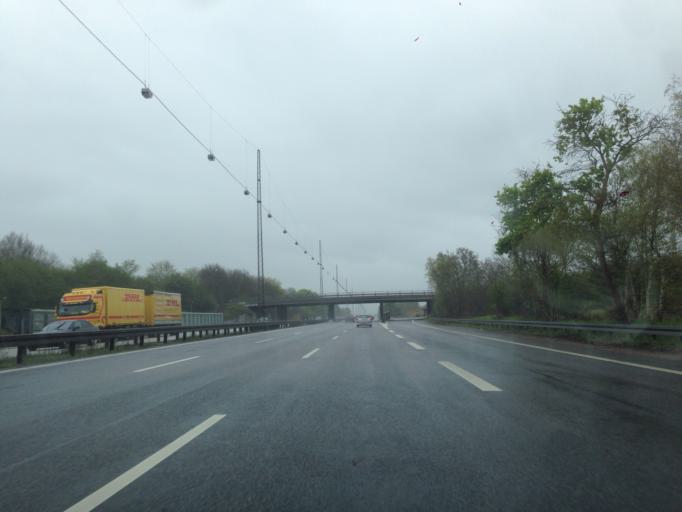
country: DK
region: Capital Region
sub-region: Lyngby-Tarbaek Kommune
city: Kongens Lyngby
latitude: 55.7892
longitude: 12.5295
